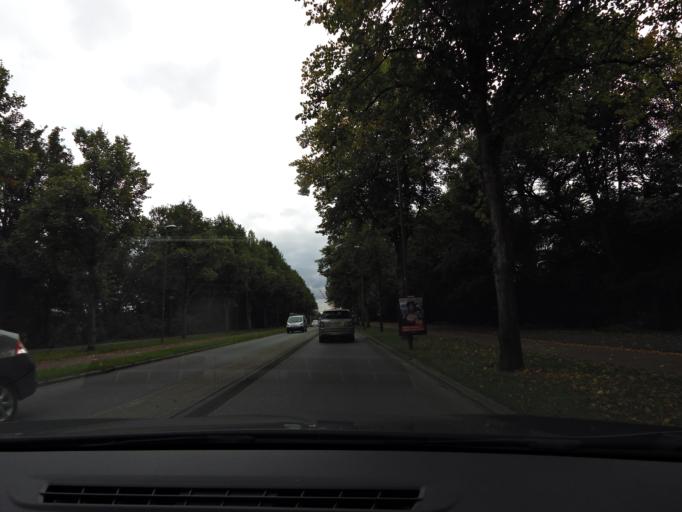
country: NL
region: South Holland
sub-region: Gemeente Schiedam
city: Schiedam
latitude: 51.9156
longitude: 4.3788
